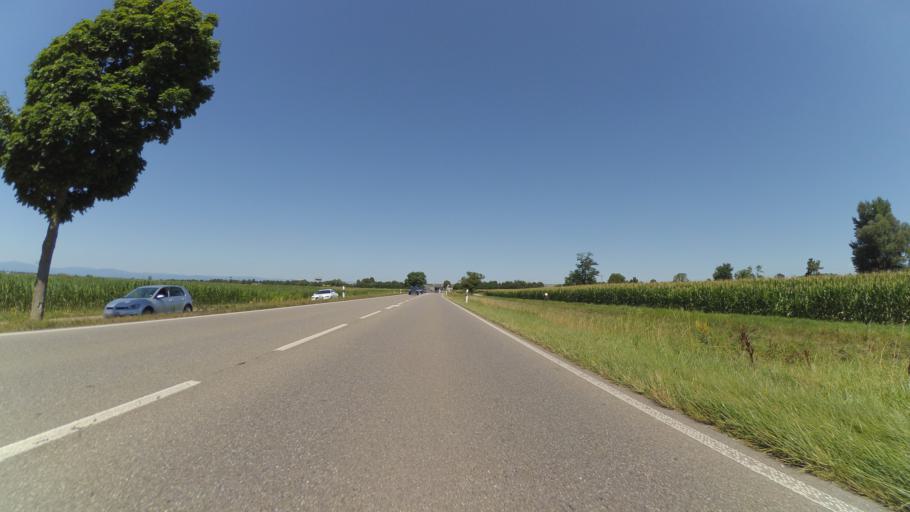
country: DE
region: Baden-Wuerttemberg
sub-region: Freiburg Region
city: Unterkrozingen
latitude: 47.9483
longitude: 7.6721
